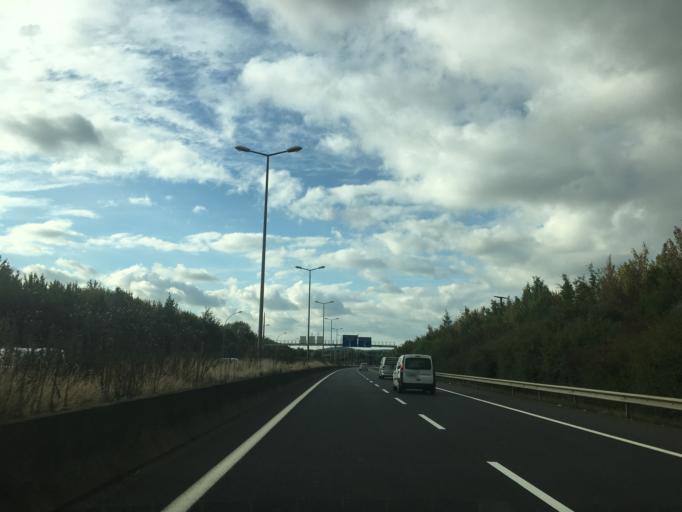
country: LU
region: Luxembourg
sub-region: Canton d'Esch-sur-Alzette
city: Schifflange
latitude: 49.5161
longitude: 6.0096
